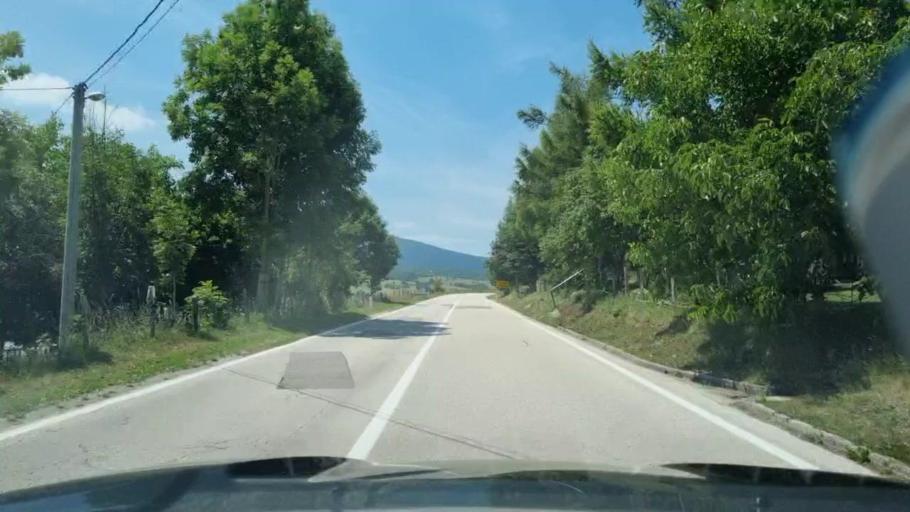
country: BA
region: Federation of Bosnia and Herzegovina
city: Sanica
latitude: 44.5474
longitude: 16.6095
